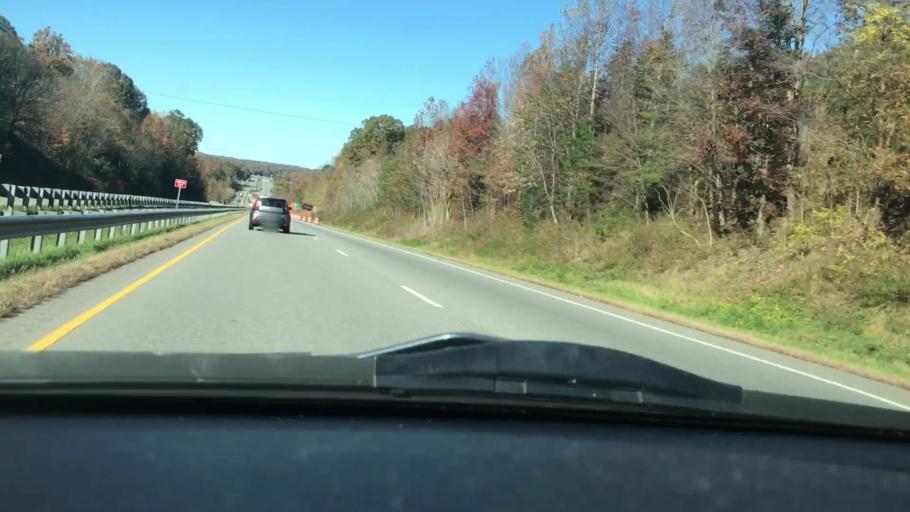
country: US
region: North Carolina
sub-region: Rockingham County
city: Stoneville
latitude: 36.4332
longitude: -79.9298
